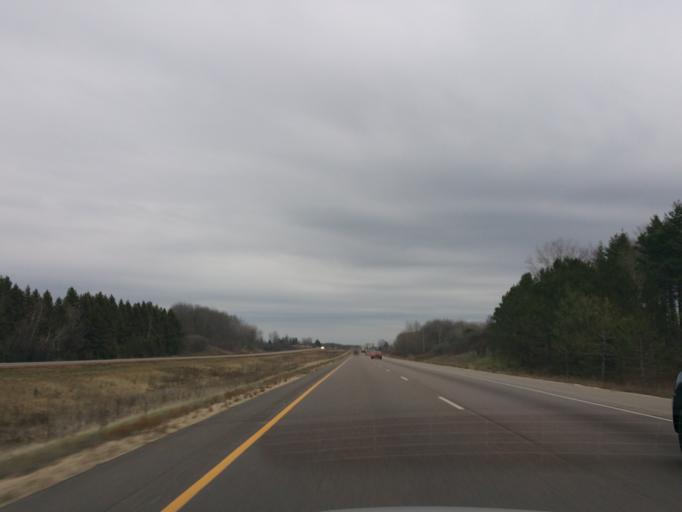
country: US
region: Wisconsin
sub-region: Pierce County
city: Spring Valley
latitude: 44.9325
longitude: -92.1578
